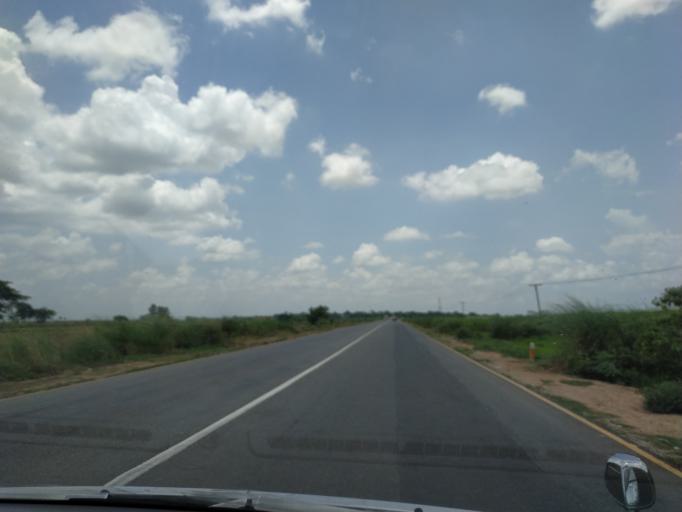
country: MM
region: Bago
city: Bago
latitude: 17.4686
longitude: 96.5691
